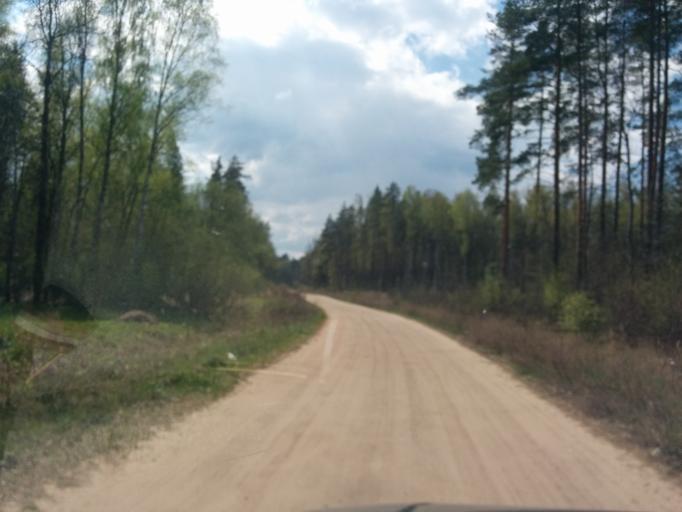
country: LV
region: Ozolnieku
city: Ozolnieki
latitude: 56.6124
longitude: 23.7838
